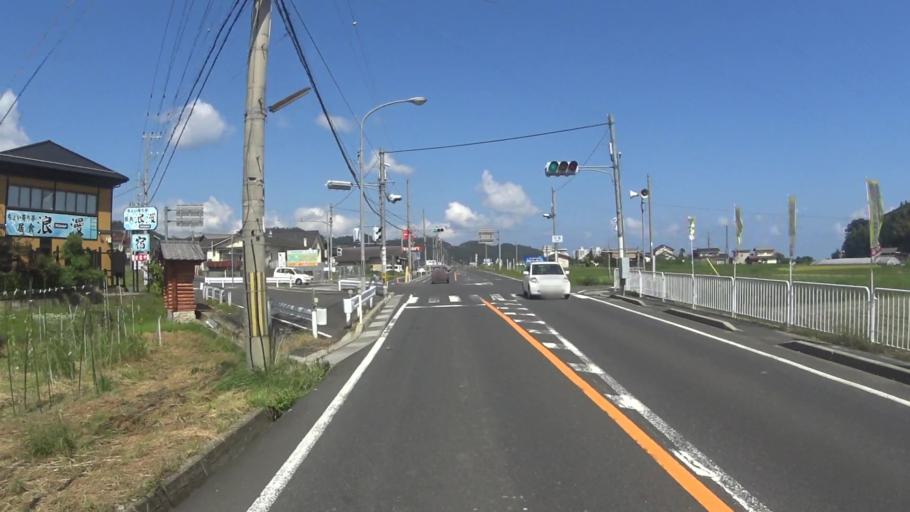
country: JP
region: Kyoto
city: Miyazu
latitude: 35.6034
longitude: 135.2207
